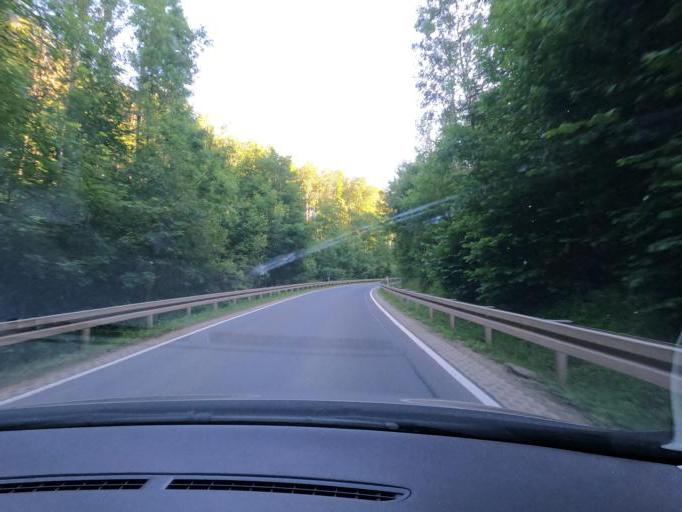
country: DE
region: Thuringia
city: Geisleden
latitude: 51.3697
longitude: 10.1982
